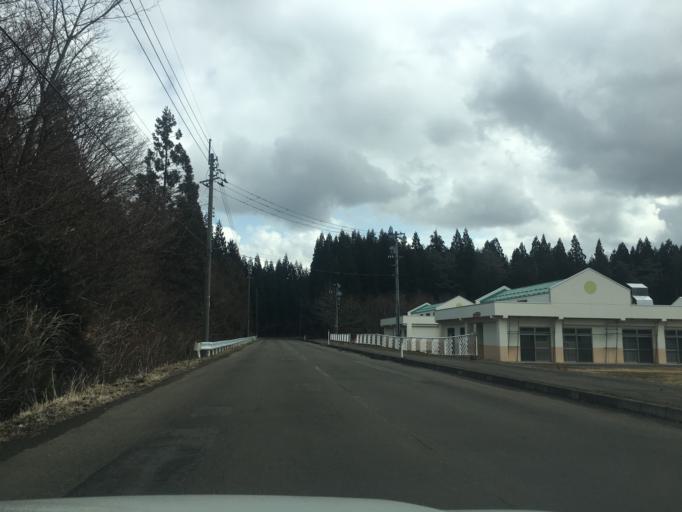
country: JP
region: Akita
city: Takanosu
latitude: 40.1867
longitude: 140.3516
